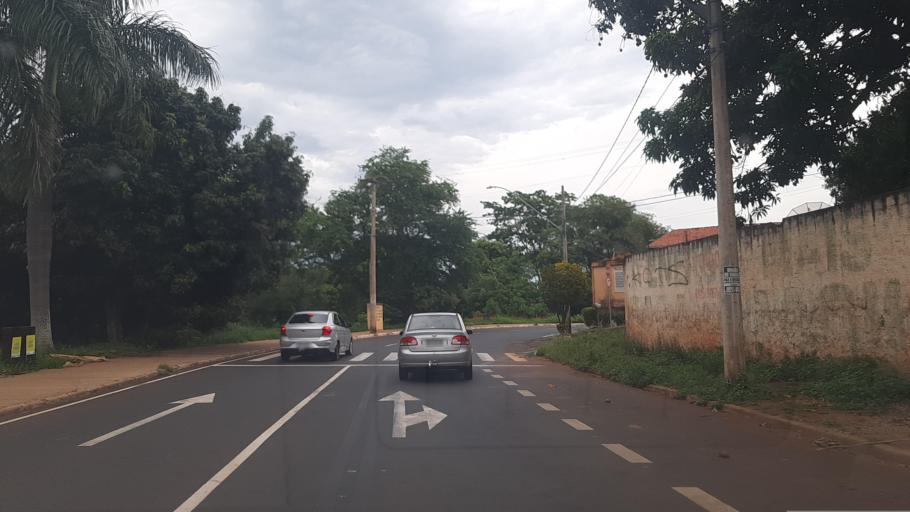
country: BR
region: Minas Gerais
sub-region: Uberlandia
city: Uberlandia
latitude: -18.9277
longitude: -48.2951
